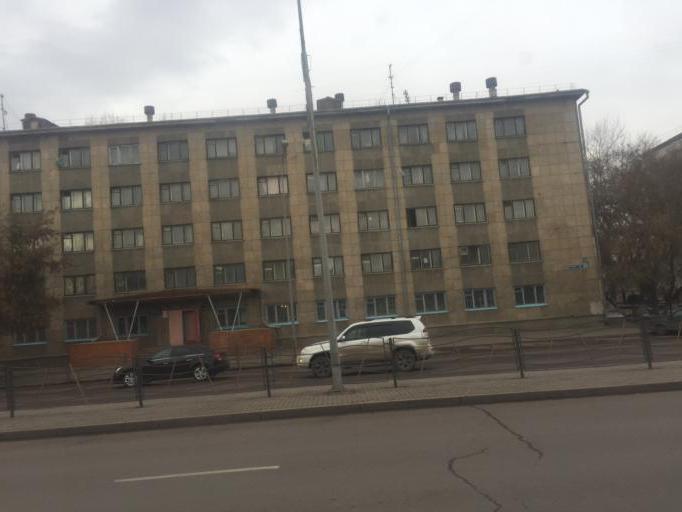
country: KZ
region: Astana Qalasy
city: Astana
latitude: 51.1762
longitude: 71.4157
